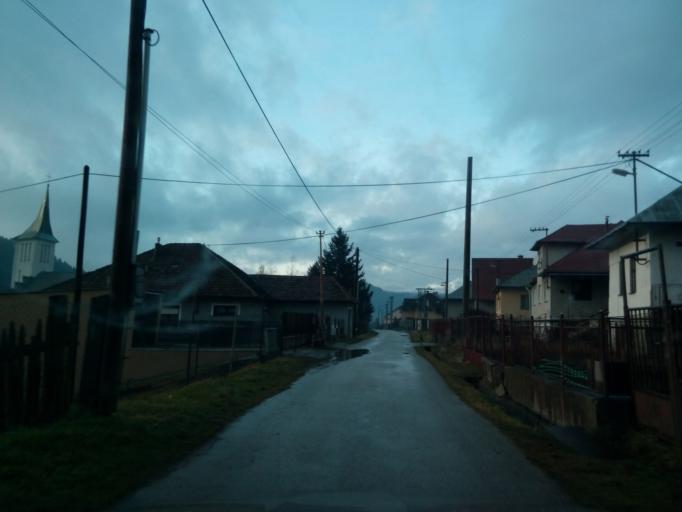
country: SK
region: Kosicky
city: Krompachy
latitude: 48.9270
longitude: 20.9232
